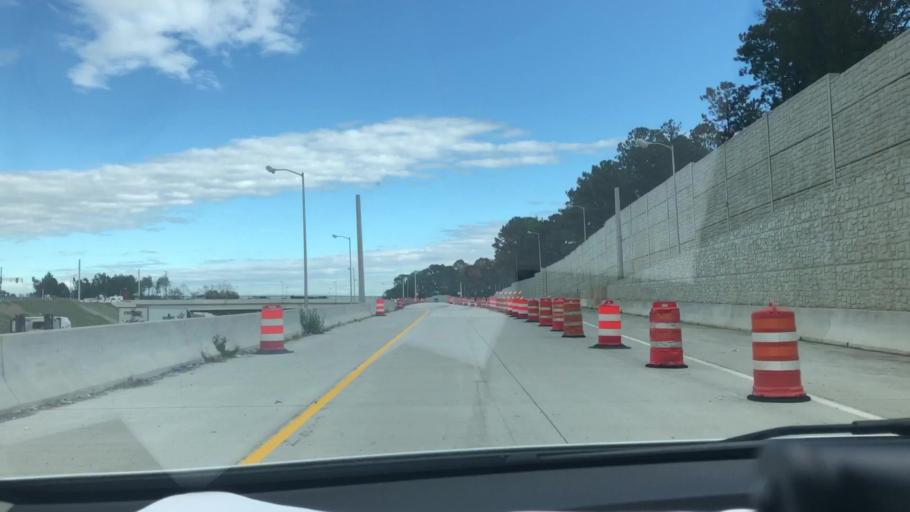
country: US
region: Georgia
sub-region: DeKalb County
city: Panthersville
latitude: 33.6986
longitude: -84.2694
